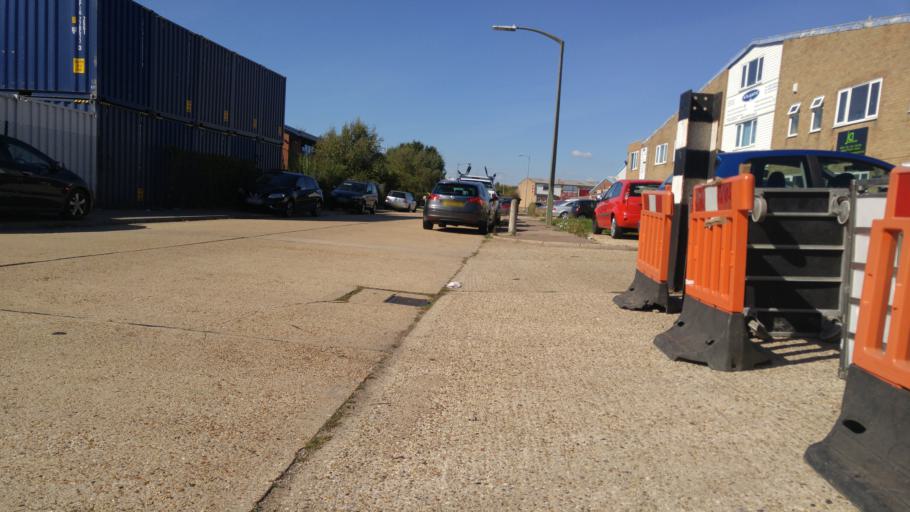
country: GB
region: England
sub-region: Essex
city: Clacton-on-Sea
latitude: 51.8158
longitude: 1.1716
